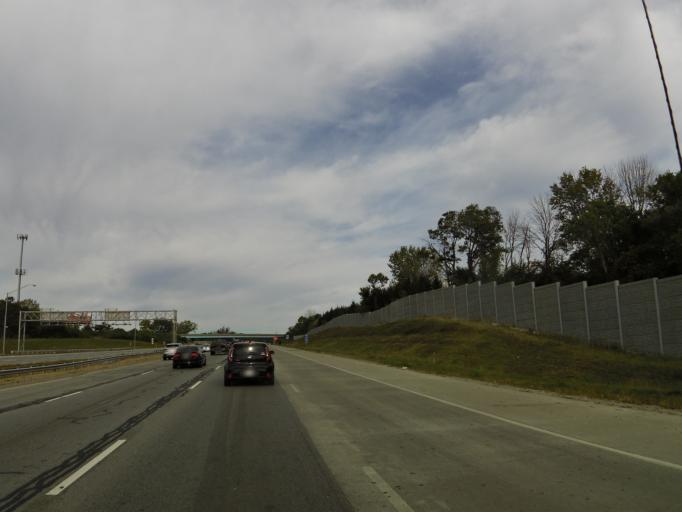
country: US
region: Indiana
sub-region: Marion County
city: Southport
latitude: 39.6684
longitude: -86.0935
